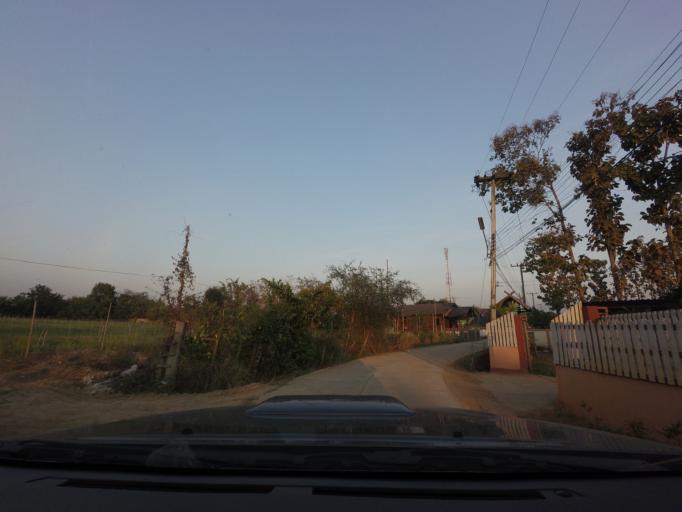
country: TH
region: Chiang Mai
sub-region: Amphoe Chiang Dao
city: Chiang Dao
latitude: 19.3678
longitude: 98.9604
